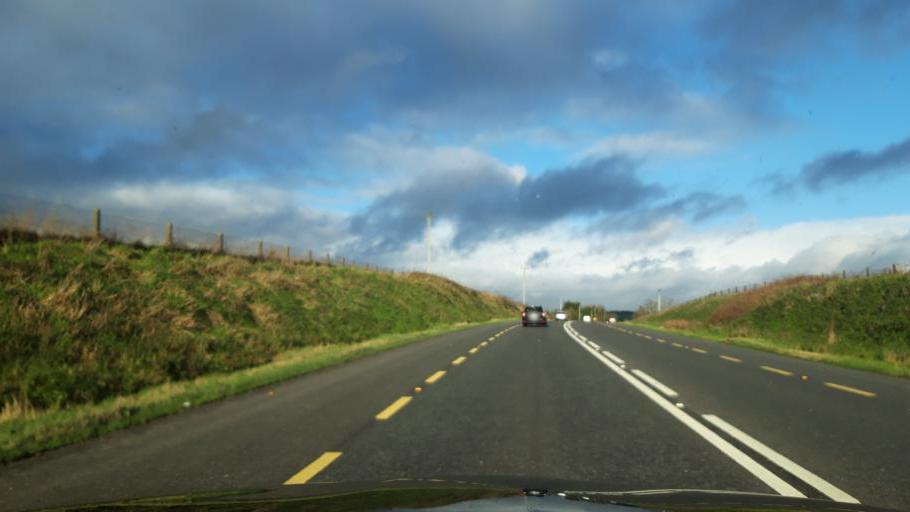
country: IE
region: Leinster
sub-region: An Mhi
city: Slane
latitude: 53.7344
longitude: -6.5133
